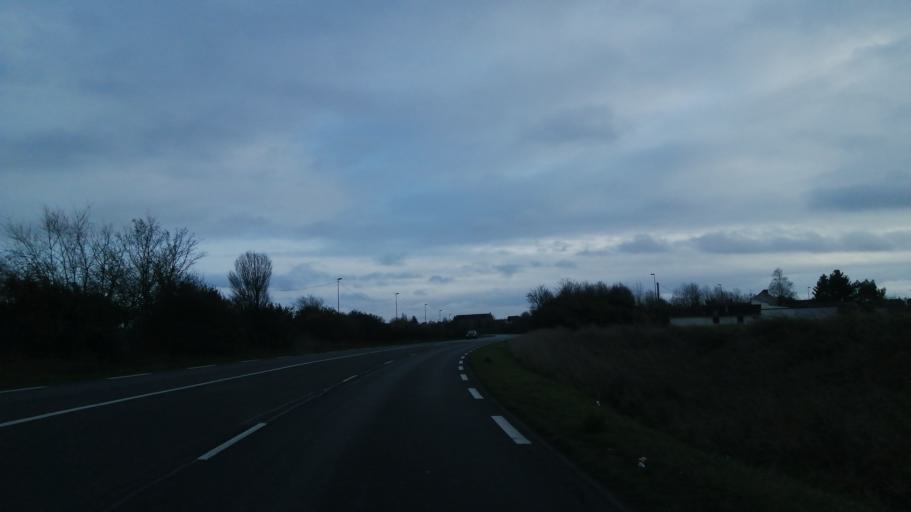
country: FR
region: Nord-Pas-de-Calais
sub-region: Departement du Pas-de-Calais
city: Rouvroy
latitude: 50.3987
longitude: 2.8951
